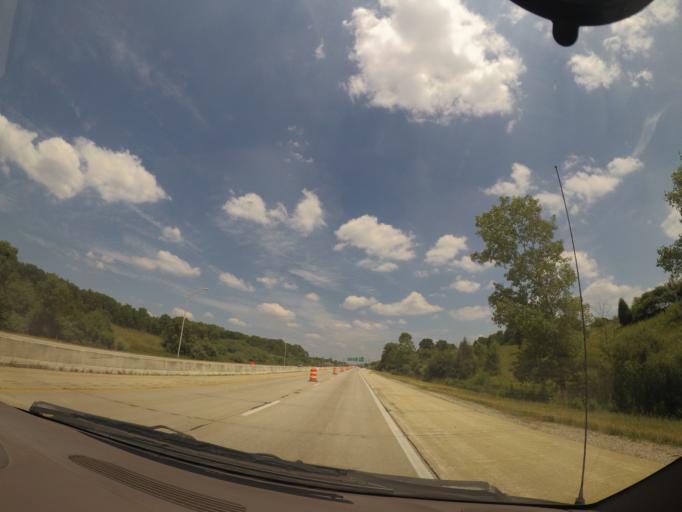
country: US
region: Indiana
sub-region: Elkhart County
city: Elkhart
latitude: 41.6290
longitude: -86.0125
